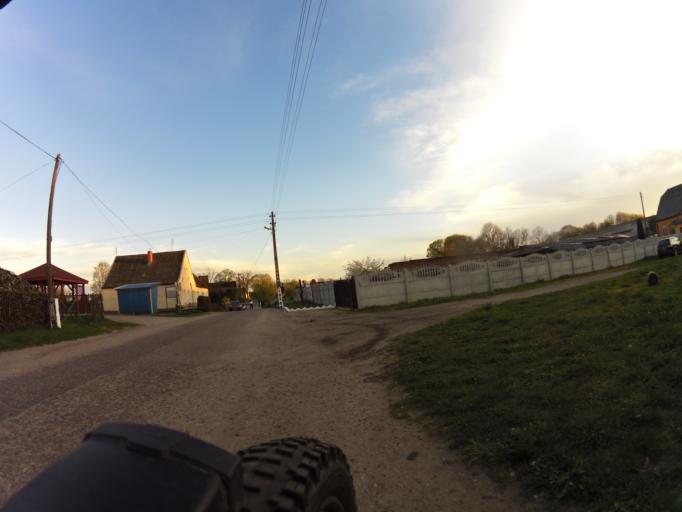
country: PL
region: West Pomeranian Voivodeship
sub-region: Powiat lobeski
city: Lobez
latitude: 53.6994
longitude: 15.6458
